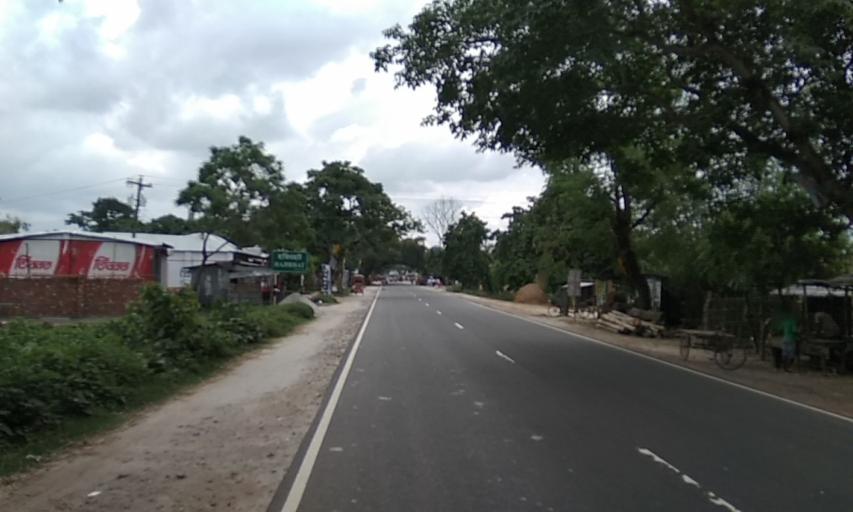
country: BD
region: Rangpur Division
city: Rangpur
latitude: 25.8005
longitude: 89.1896
